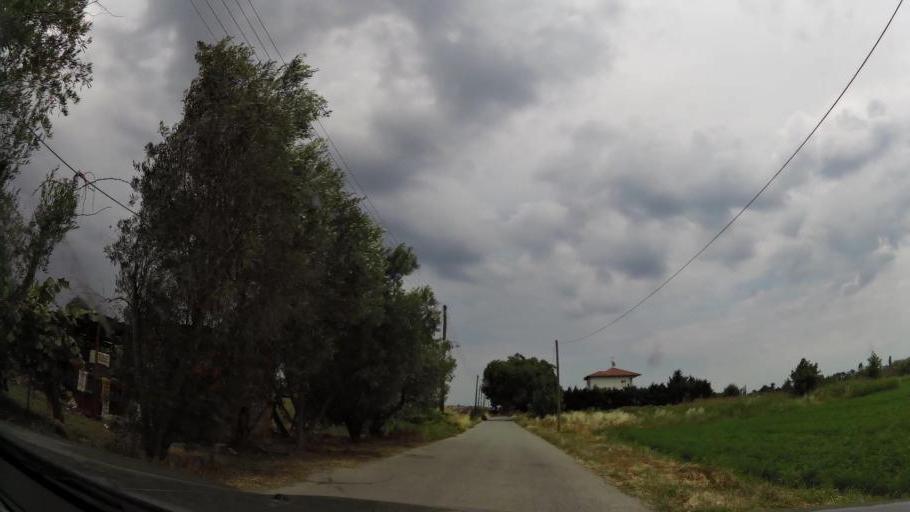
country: GR
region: Central Macedonia
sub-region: Nomos Pierias
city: Kallithea
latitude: 40.2739
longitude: 22.5843
